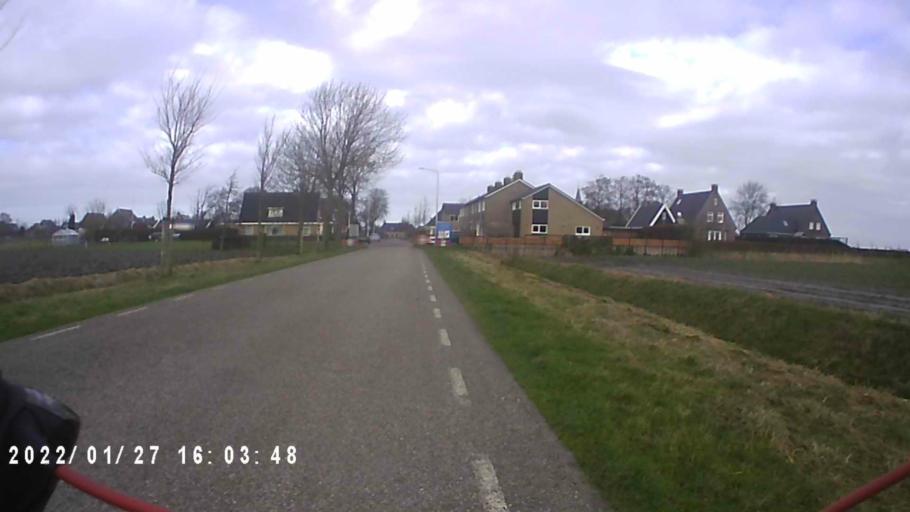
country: NL
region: Friesland
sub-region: Gemeente Dongeradeel
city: Anjum
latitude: 53.3787
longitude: 6.0889
